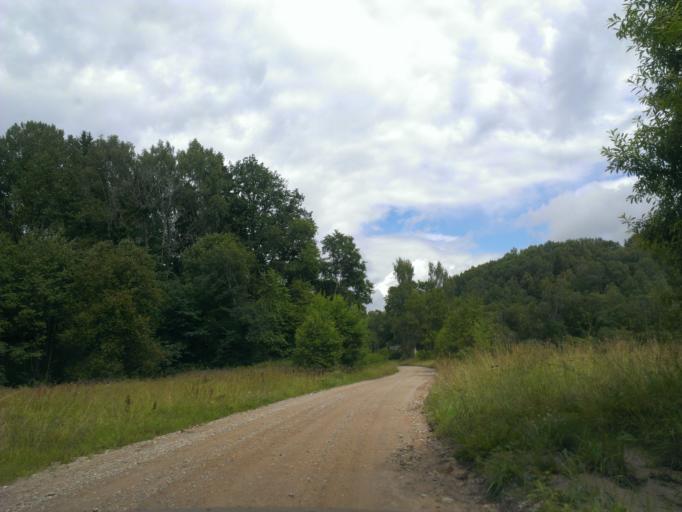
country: LV
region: Ligatne
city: Ligatne
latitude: 57.2081
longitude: 25.0063
